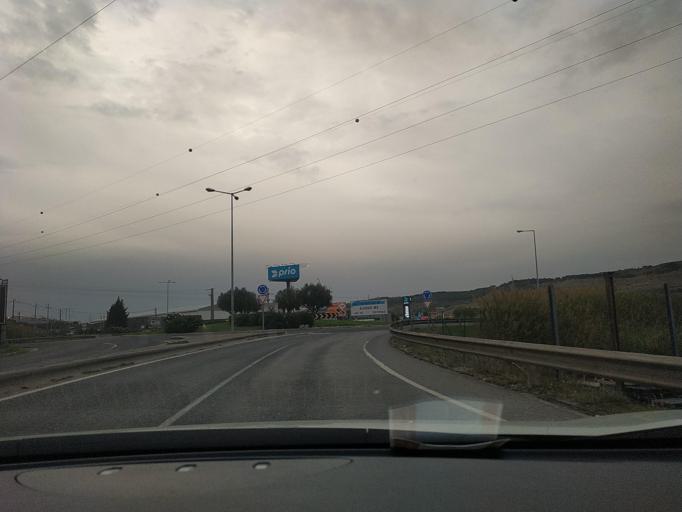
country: PT
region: Lisbon
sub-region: Loures
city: Santo Antao do Tojal
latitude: 38.8607
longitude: -9.1156
